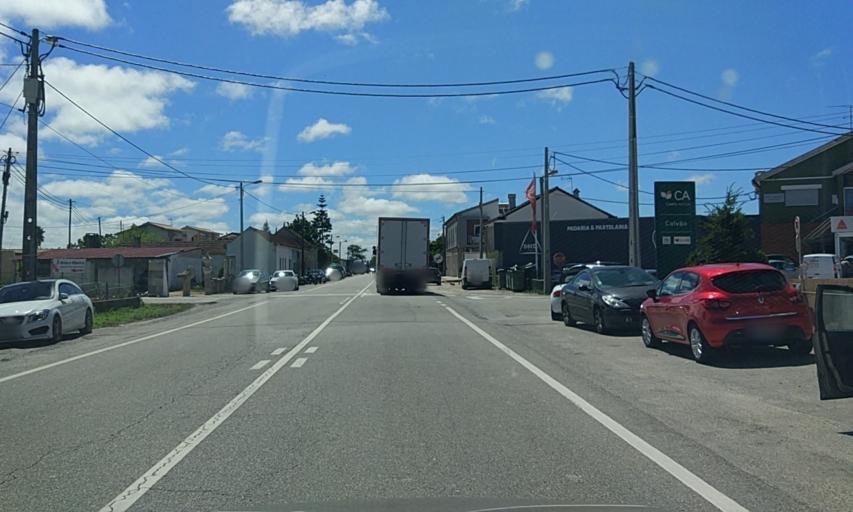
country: PT
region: Coimbra
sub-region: Mira
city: Mira
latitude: 40.4750
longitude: -8.6962
